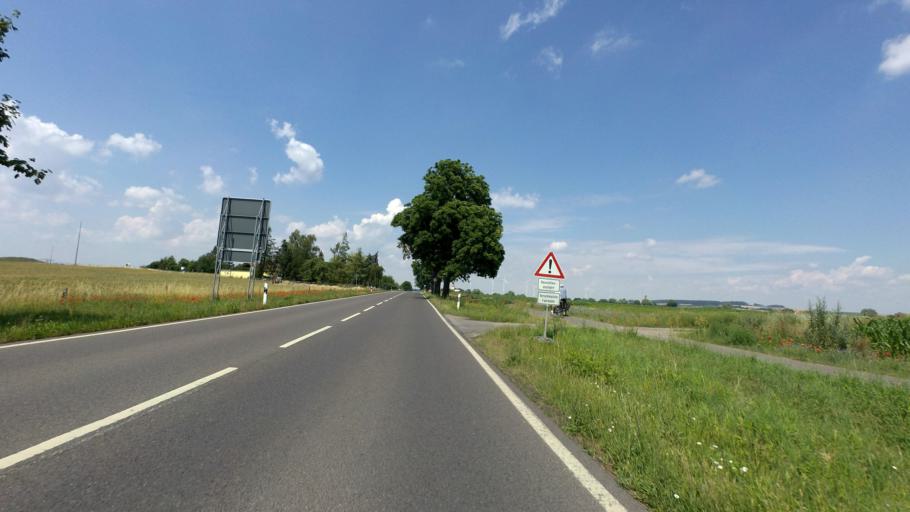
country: DE
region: Brandenburg
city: Angermunde
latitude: 53.0307
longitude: 13.9926
